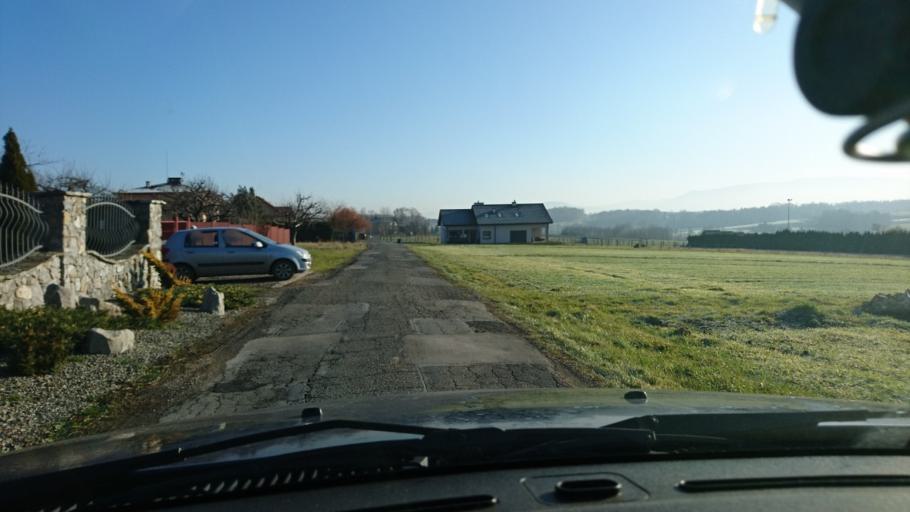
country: PL
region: Silesian Voivodeship
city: Janowice
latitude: 49.8981
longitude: 19.0954
